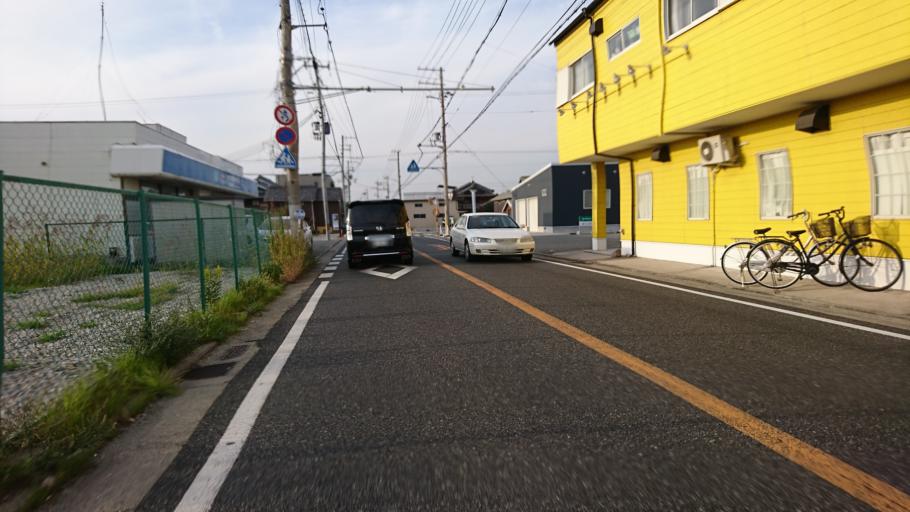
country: JP
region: Hyogo
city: Kakogawacho-honmachi
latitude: 34.7362
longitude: 134.8287
